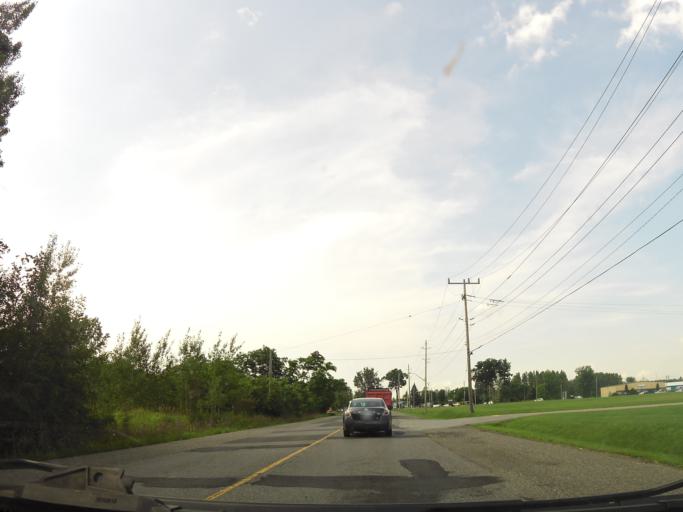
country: CA
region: Ontario
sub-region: Lanark County
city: Smiths Falls
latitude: 44.9039
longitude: -76.0308
